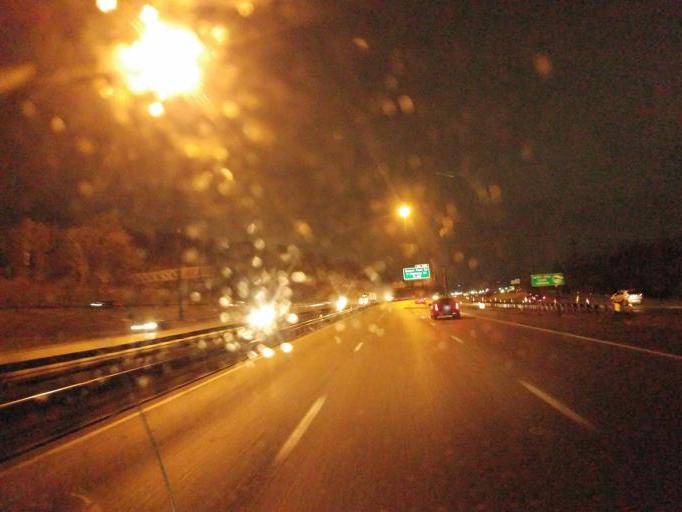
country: US
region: Missouri
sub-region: Saint Louis County
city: Sunset Hills
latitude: 38.5465
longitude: -90.4294
